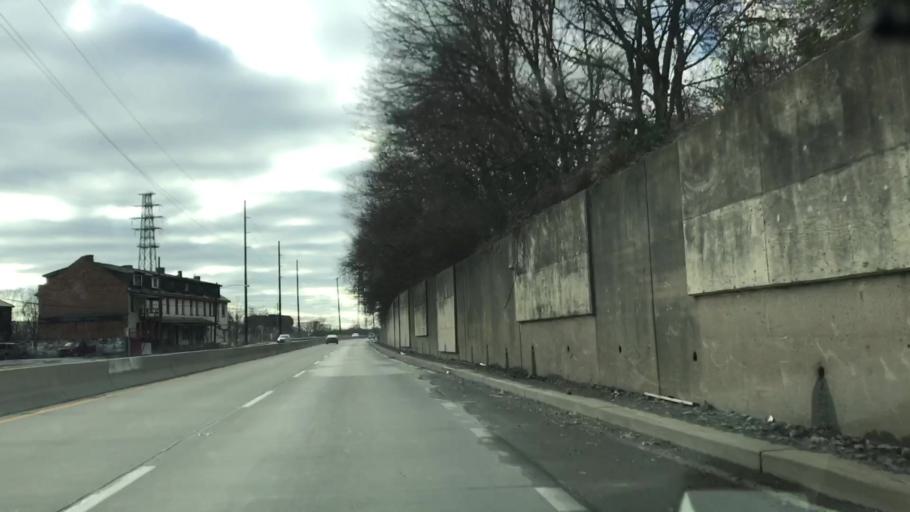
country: US
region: Pennsylvania
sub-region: Beaver County
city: Aliquippa
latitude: 40.6170
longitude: -80.2433
